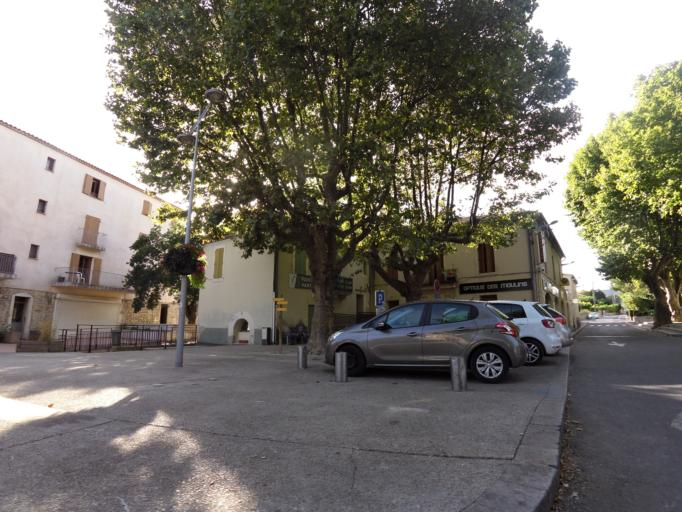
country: FR
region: Languedoc-Roussillon
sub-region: Departement du Gard
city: Calvisson
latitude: 43.7859
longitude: 4.1932
